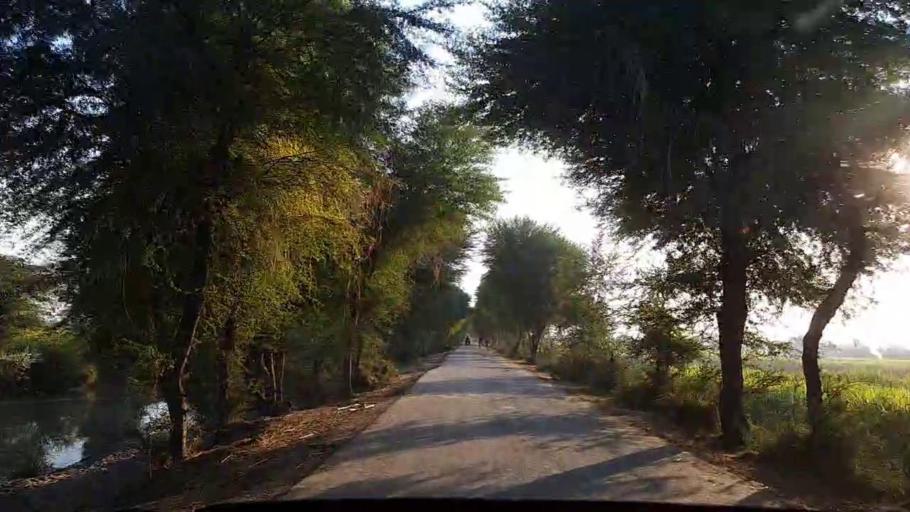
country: PK
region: Sindh
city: Sobhadero
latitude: 27.3984
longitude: 68.3882
